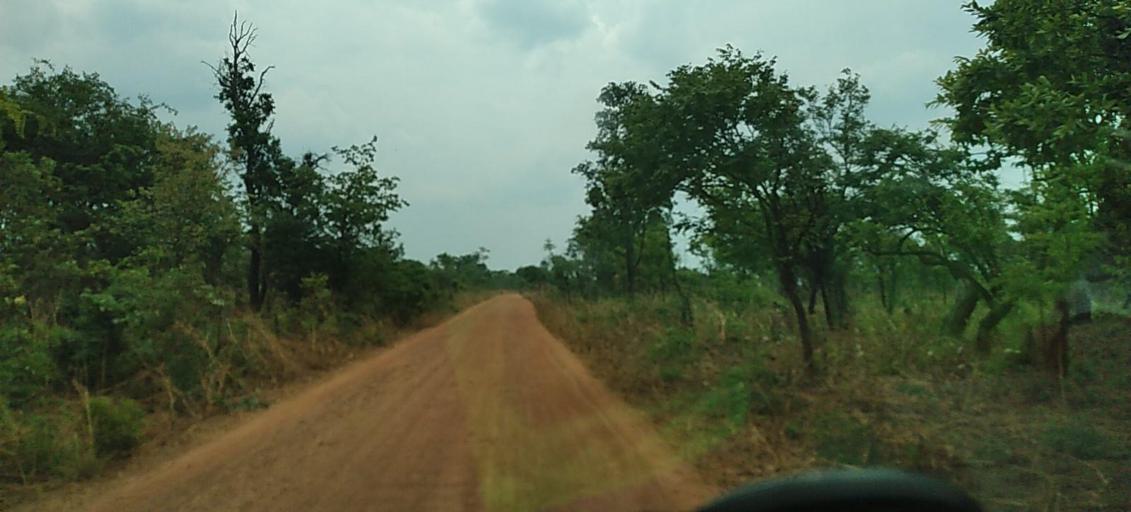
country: ZM
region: North-Western
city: Kansanshi
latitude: -12.0816
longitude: 26.3601
